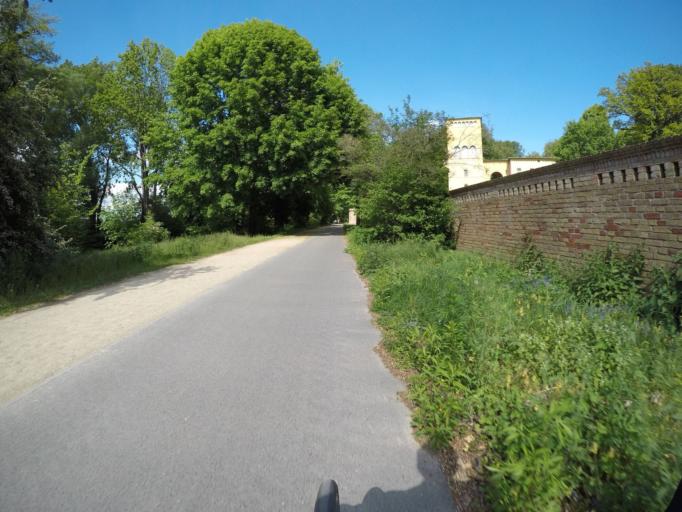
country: DE
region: Brandenburg
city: Potsdam
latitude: 52.4161
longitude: 13.0937
